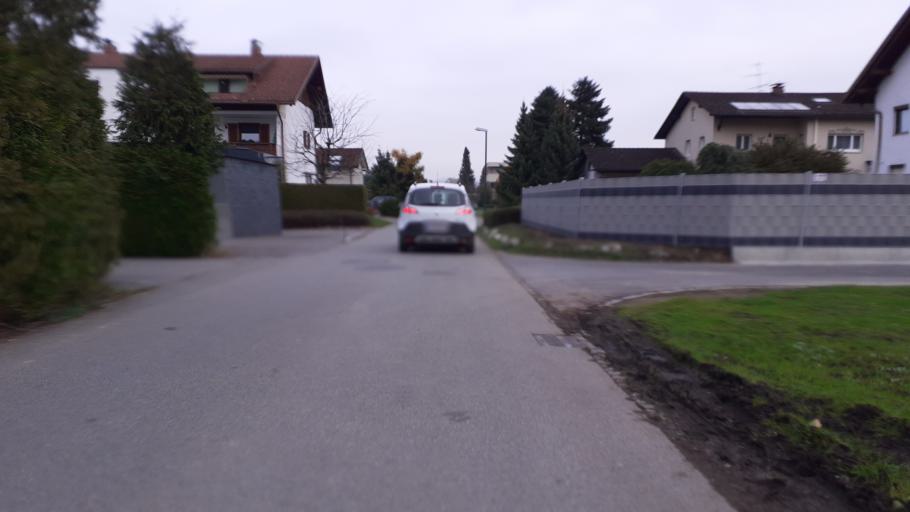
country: AT
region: Vorarlberg
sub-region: Politischer Bezirk Feldkirch
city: Nofels
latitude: 47.2588
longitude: 9.5865
